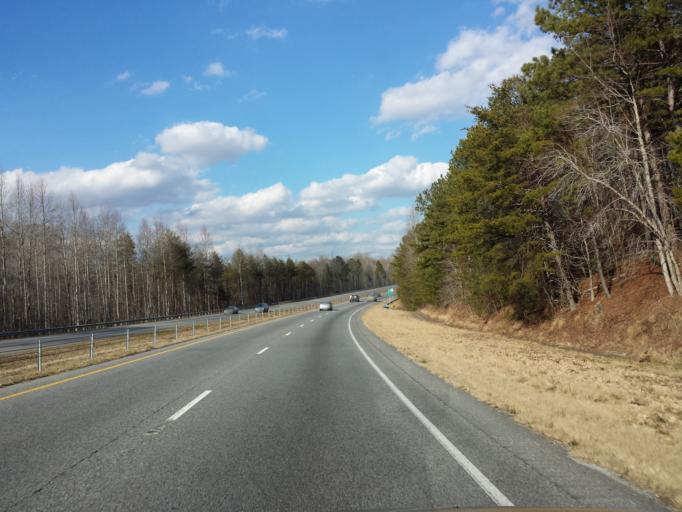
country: US
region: Georgia
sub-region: Lumpkin County
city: Dahlonega
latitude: 34.4378
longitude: -83.9936
